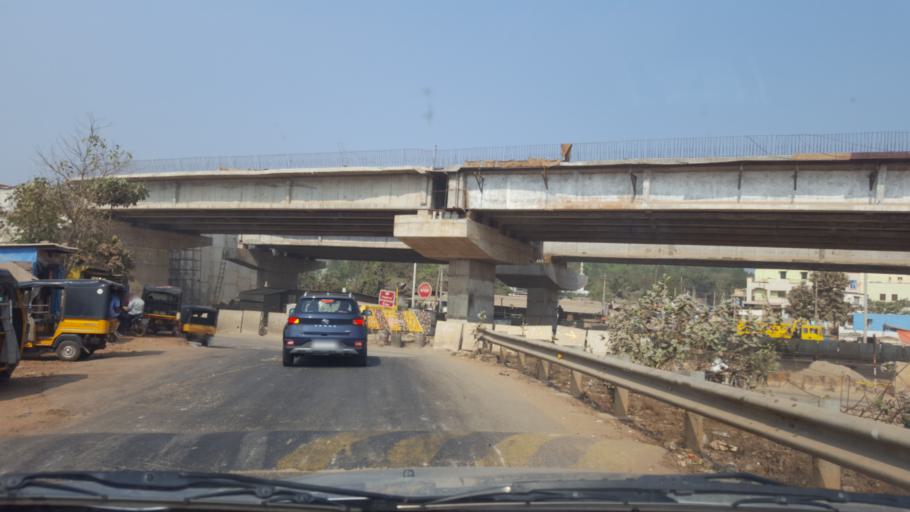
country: IN
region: Andhra Pradesh
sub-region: Vishakhapatnam
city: Bhimunipatnam
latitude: 17.8941
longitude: 83.3773
